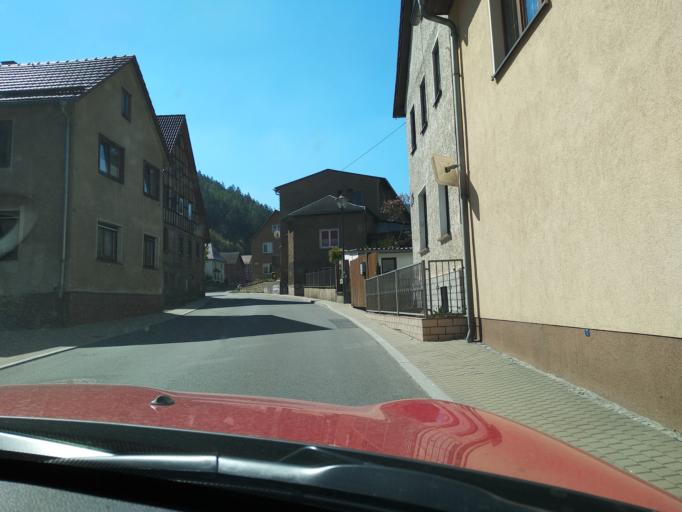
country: DE
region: Thuringia
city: Bad Blankenburg
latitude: 50.6648
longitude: 11.2907
